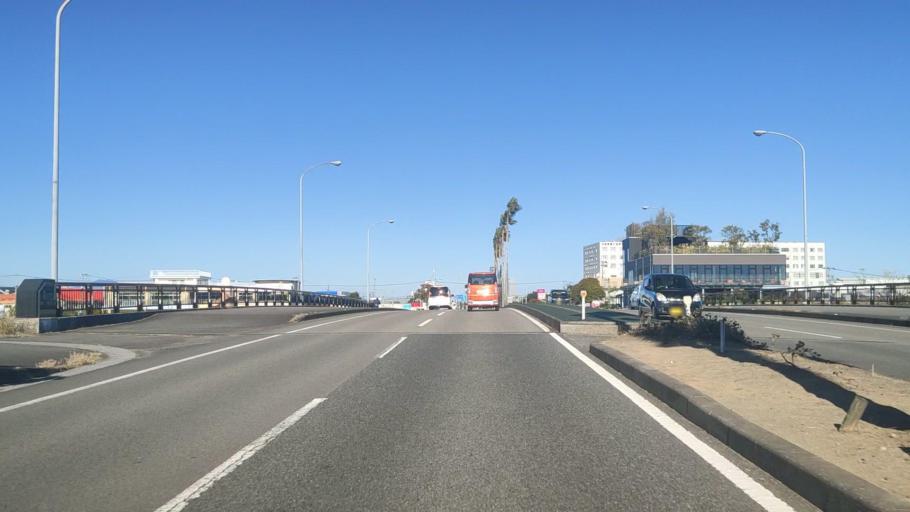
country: JP
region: Miyazaki
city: Miyazaki-shi
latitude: 31.9192
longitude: 131.4509
